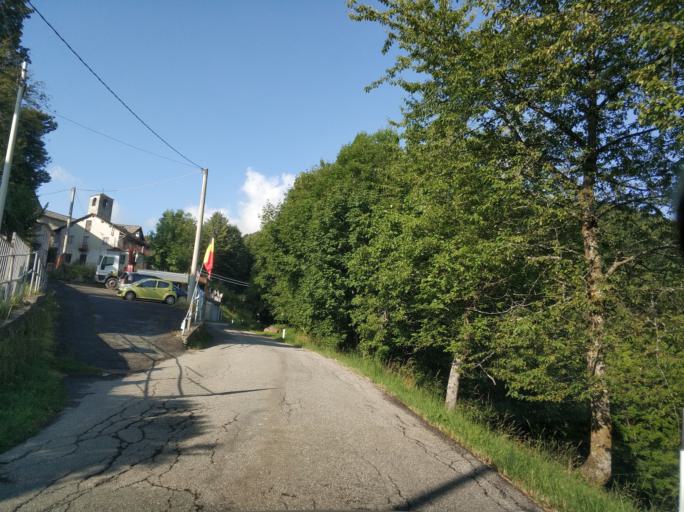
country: IT
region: Piedmont
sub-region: Provincia di Torino
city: Viu
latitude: 45.2169
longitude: 7.3786
